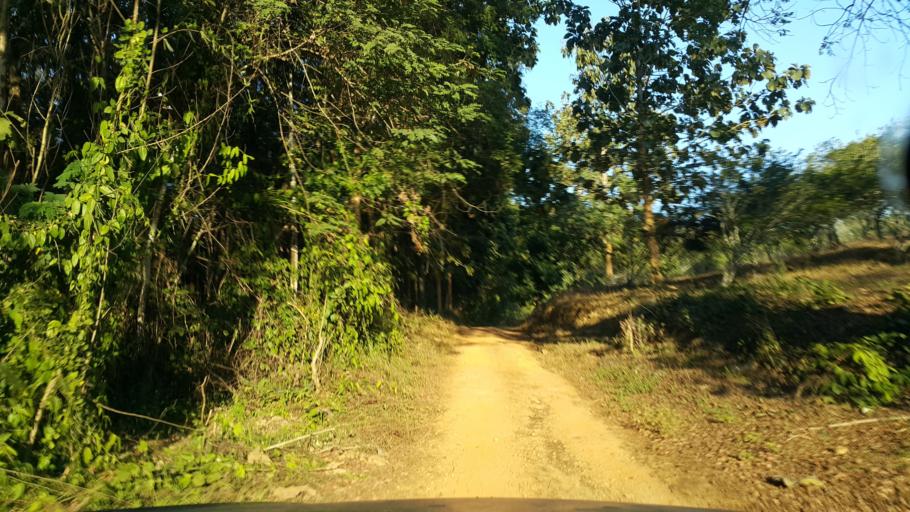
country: TH
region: Sukhothai
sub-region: Amphoe Si Satchanalai
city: Si Satchanalai
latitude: 17.5841
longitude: 99.6061
